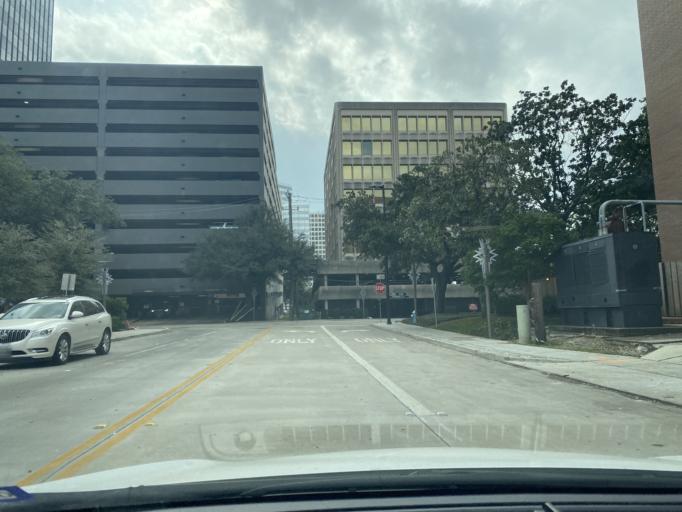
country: US
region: Texas
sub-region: Harris County
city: West University Place
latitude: 29.7507
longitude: -95.4578
